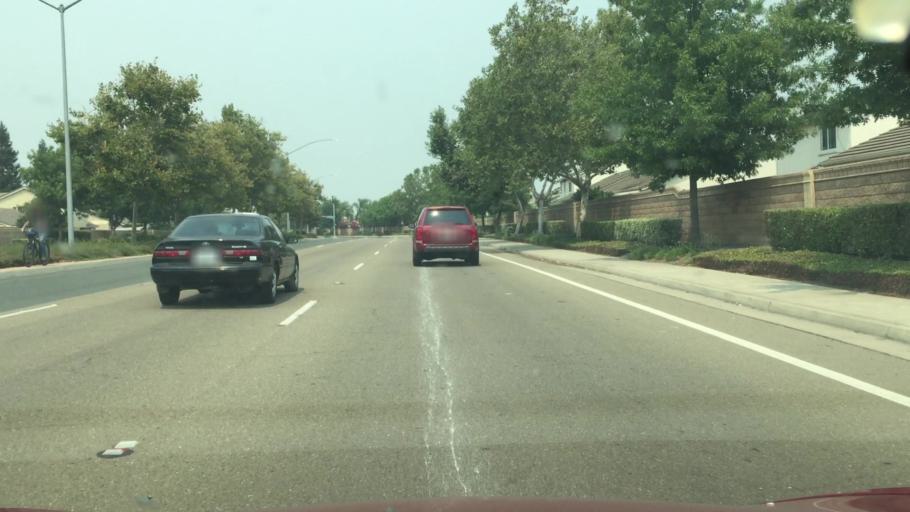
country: US
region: California
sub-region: San Joaquin County
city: Morada
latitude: 38.0251
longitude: -121.2705
